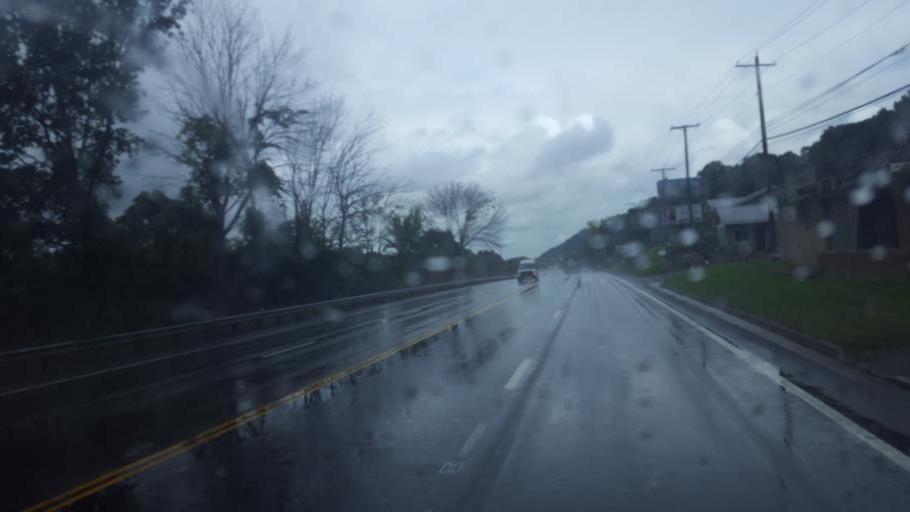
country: US
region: Ohio
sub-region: Scioto County
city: Rosemount
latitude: 38.7751
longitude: -82.9853
